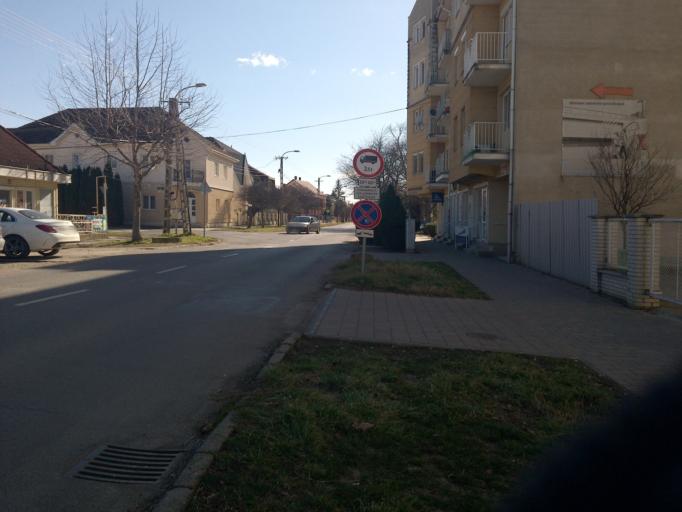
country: HU
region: Hajdu-Bihar
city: Hajduszoboszlo
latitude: 47.4475
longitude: 21.3987
